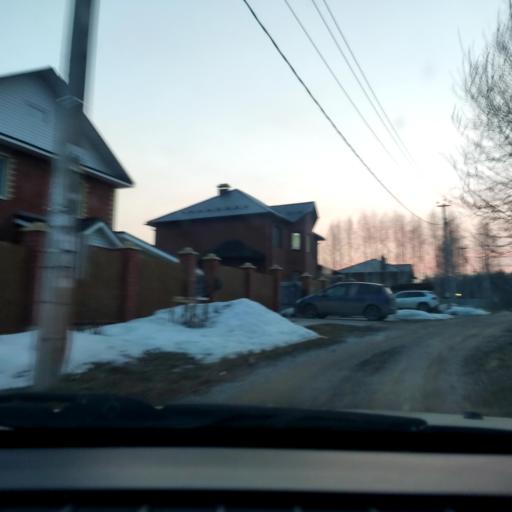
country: RU
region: Perm
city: Kondratovo
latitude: 58.0589
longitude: 56.0127
